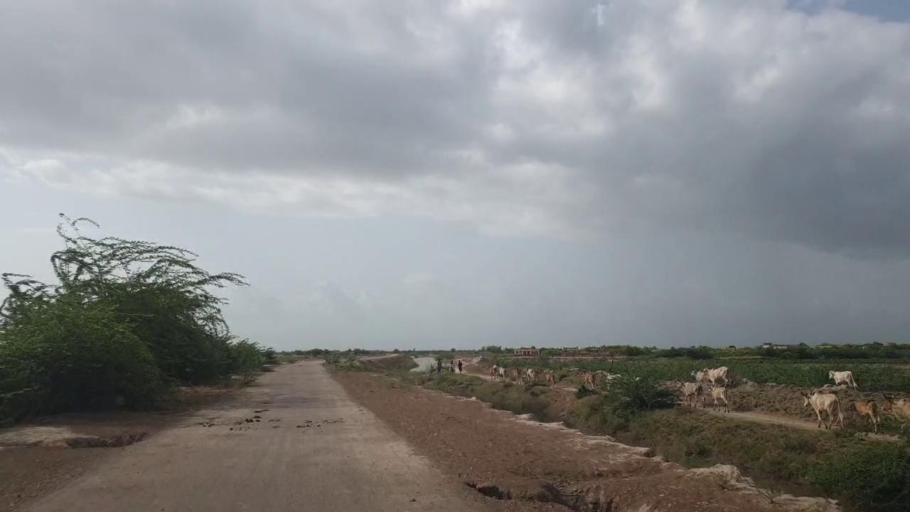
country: PK
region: Sindh
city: Kadhan
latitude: 24.5668
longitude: 69.0631
